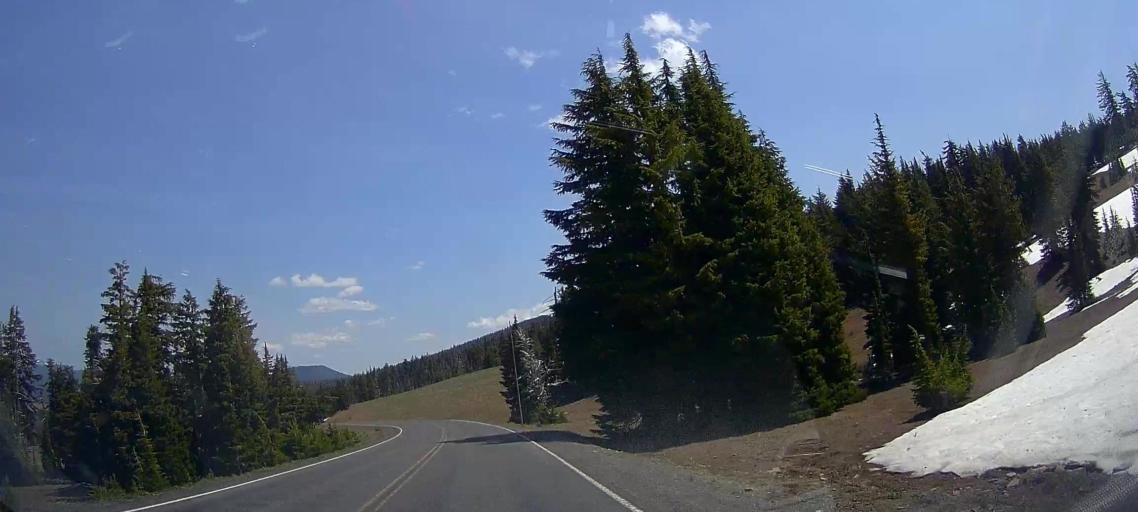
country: US
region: Oregon
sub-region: Jackson County
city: Shady Cove
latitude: 42.9833
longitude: -122.1510
